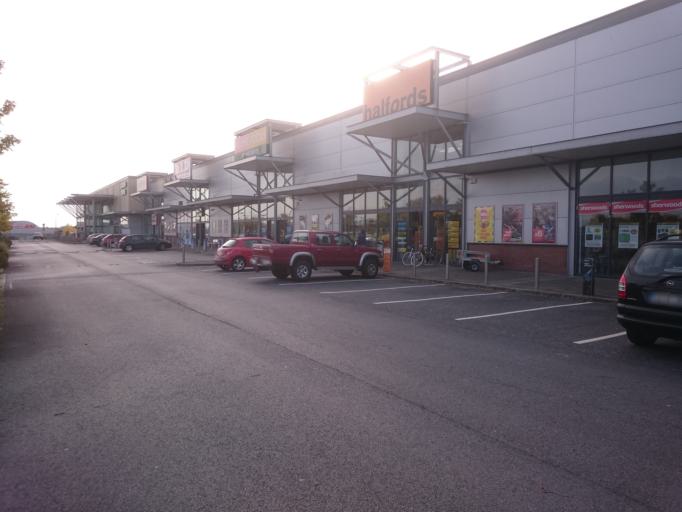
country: IE
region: Leinster
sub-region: Kilkenny
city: Kilkenny
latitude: 52.6346
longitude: -7.2457
